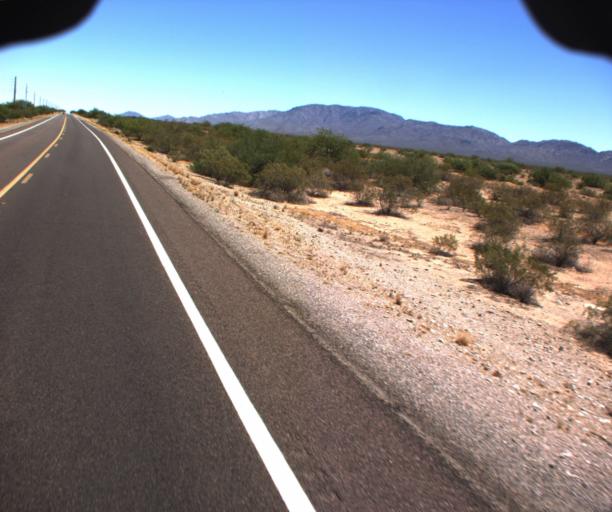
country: US
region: Arizona
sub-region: La Paz County
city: Salome
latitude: 33.8236
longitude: -113.5274
